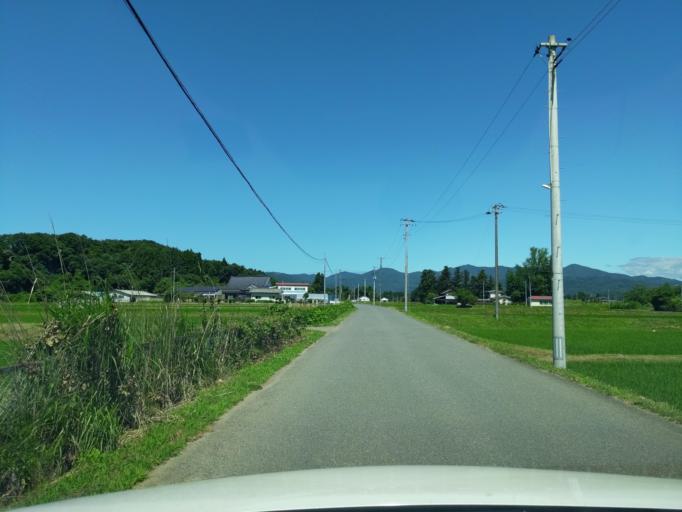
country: JP
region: Fukushima
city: Koriyama
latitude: 37.3865
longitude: 140.2910
